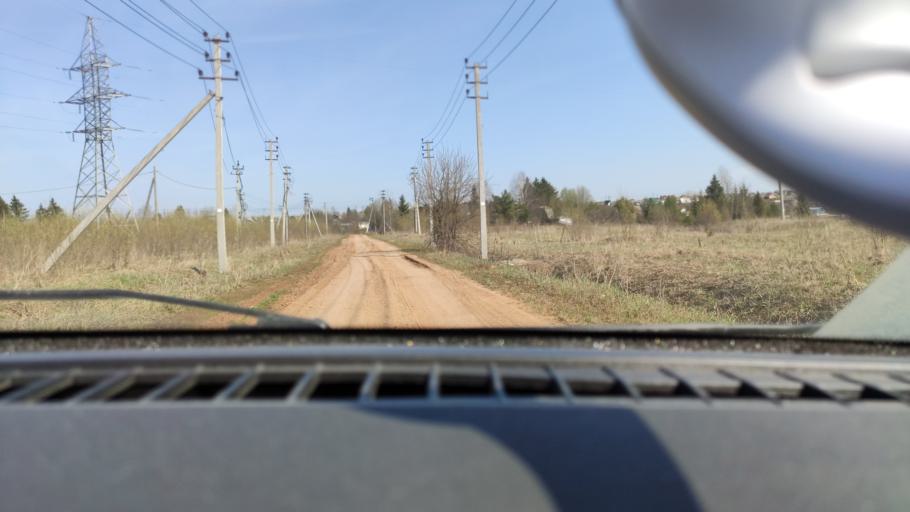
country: RU
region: Perm
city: Kultayevo
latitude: 57.8910
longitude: 55.8655
